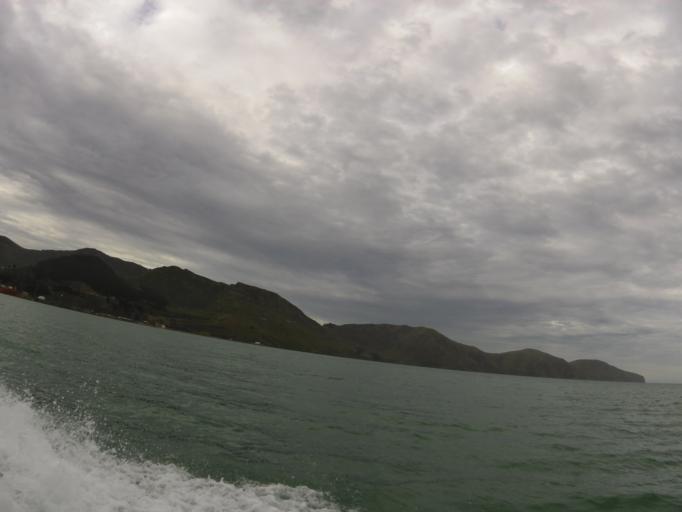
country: NZ
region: Canterbury
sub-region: Christchurch City
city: Christchurch
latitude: -43.6225
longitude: 172.7351
